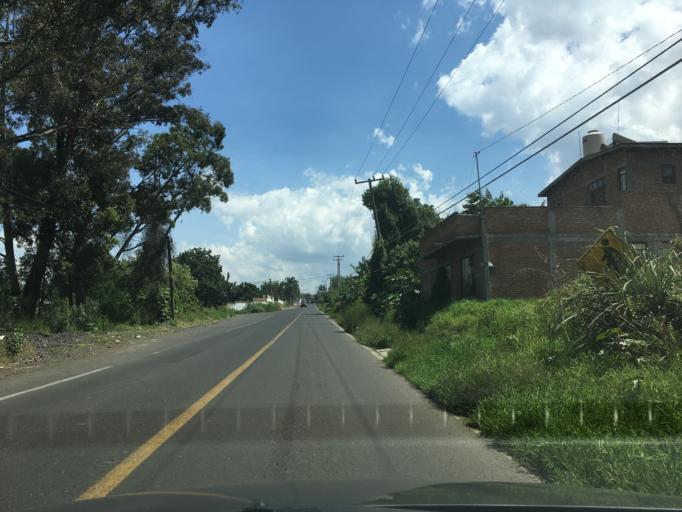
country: MX
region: Michoacan
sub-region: Morelia
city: La Mintzita (Piedra Dura)
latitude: 19.6398
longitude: -101.2686
